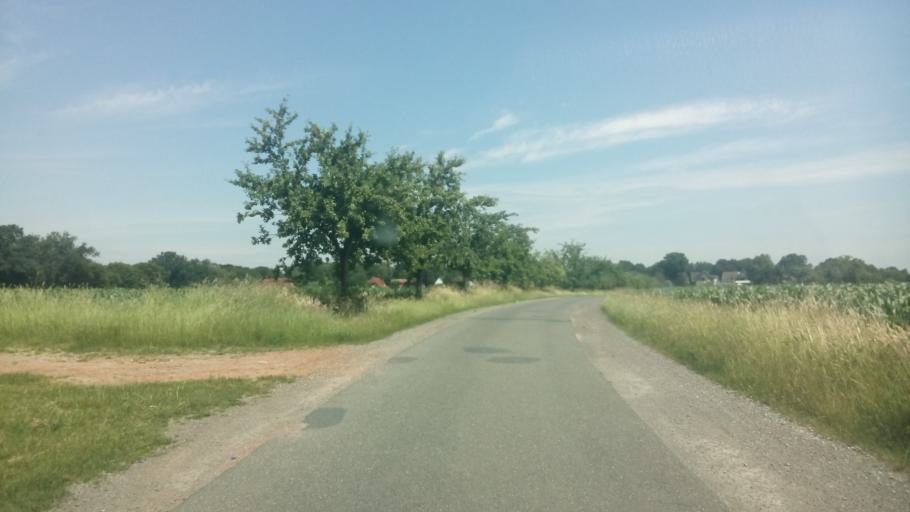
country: DE
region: Lower Saxony
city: Osterholz-Scharmbeck
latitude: 53.2575
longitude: 8.8192
